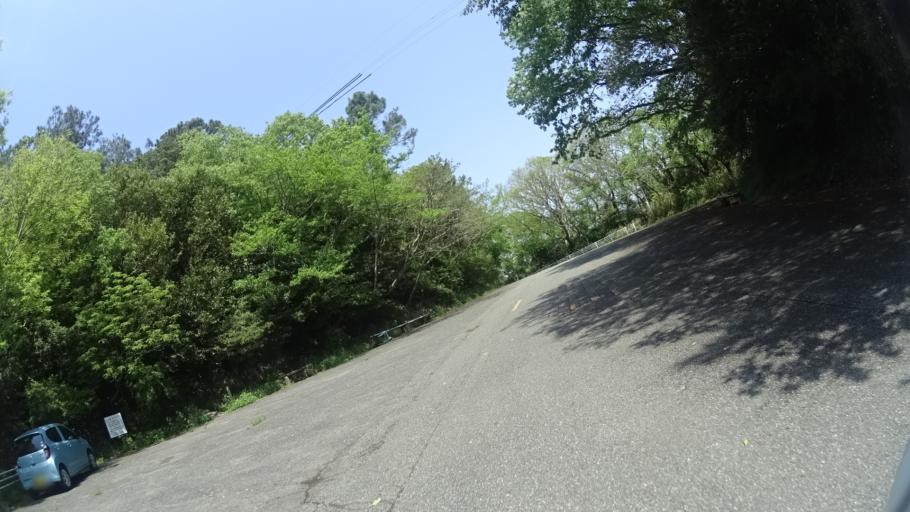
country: JP
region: Tokushima
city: Tokushima-shi
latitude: 34.0666
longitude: 134.5269
